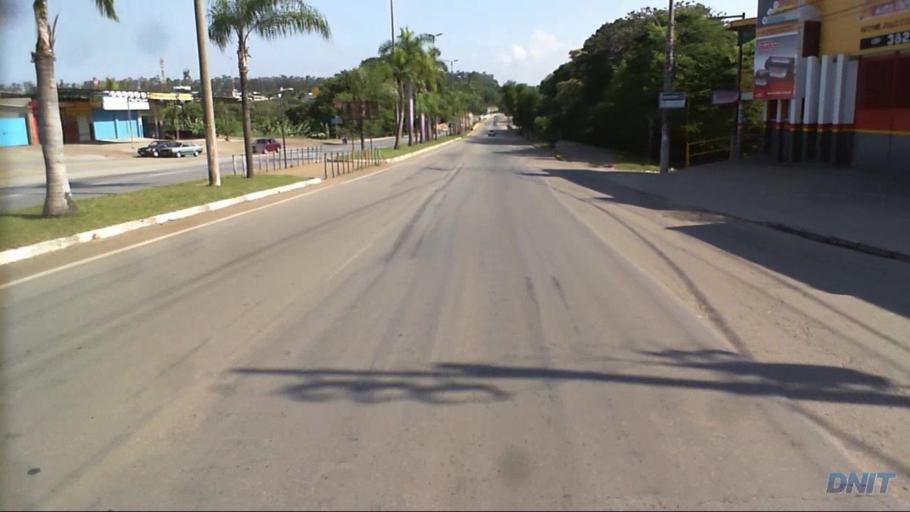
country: BR
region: Minas Gerais
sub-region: Ipatinga
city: Ipatinga
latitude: -19.4664
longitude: -42.5360
